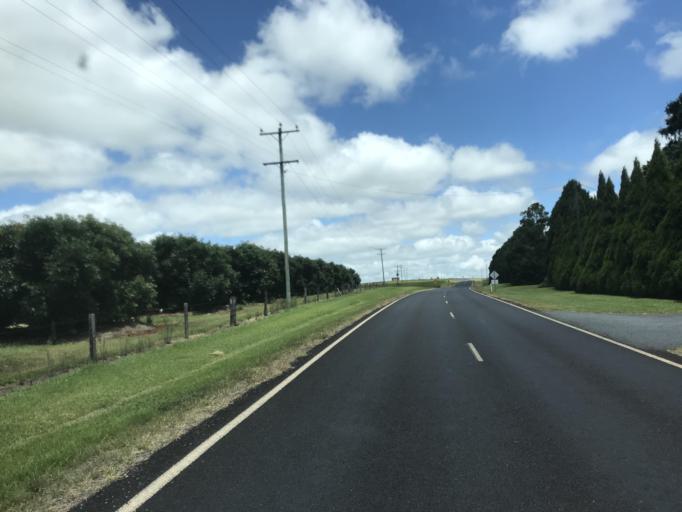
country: AU
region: Queensland
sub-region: Tablelands
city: Ravenshoe
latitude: -17.5084
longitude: 145.4688
